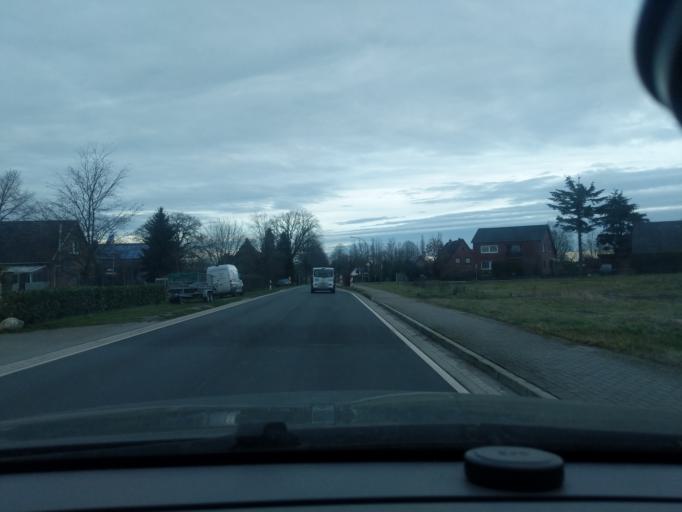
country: DE
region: Lower Saxony
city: Sauensiek
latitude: 53.3881
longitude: 9.6016
